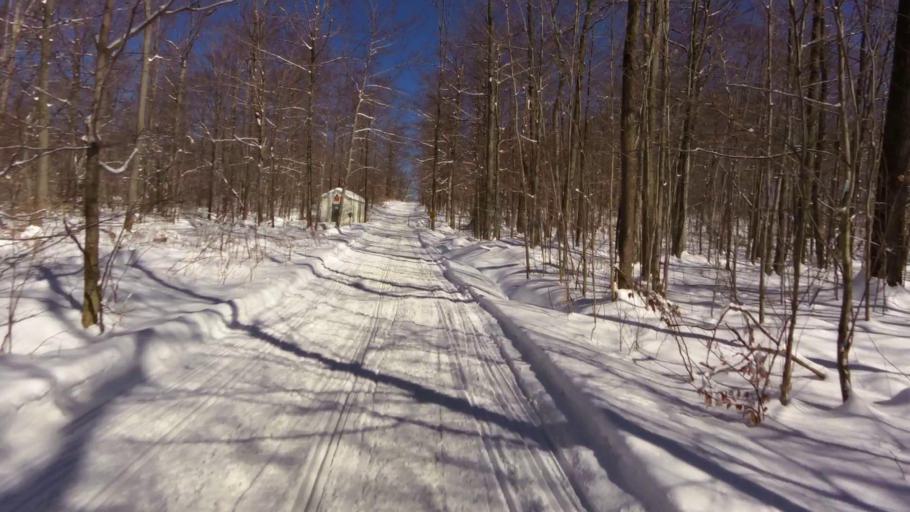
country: US
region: New York
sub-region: Chautauqua County
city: Mayville
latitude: 42.2738
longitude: -79.4589
